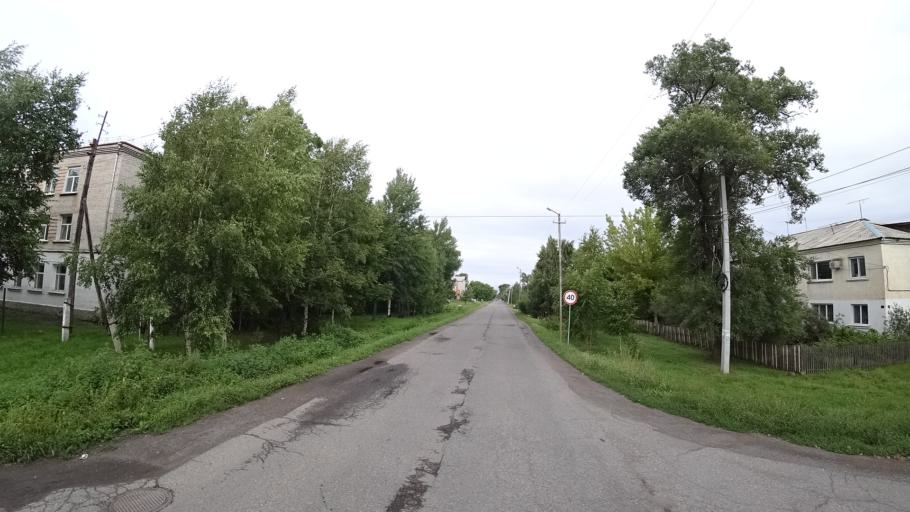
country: RU
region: Primorskiy
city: Chernigovka
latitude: 44.3377
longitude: 132.5801
